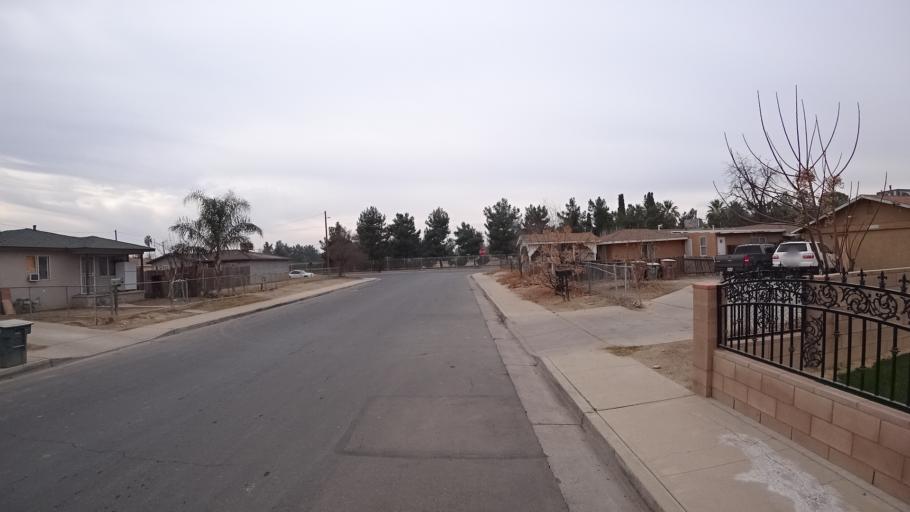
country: US
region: California
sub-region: Kern County
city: Bakersfield
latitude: 35.3622
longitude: -118.9903
